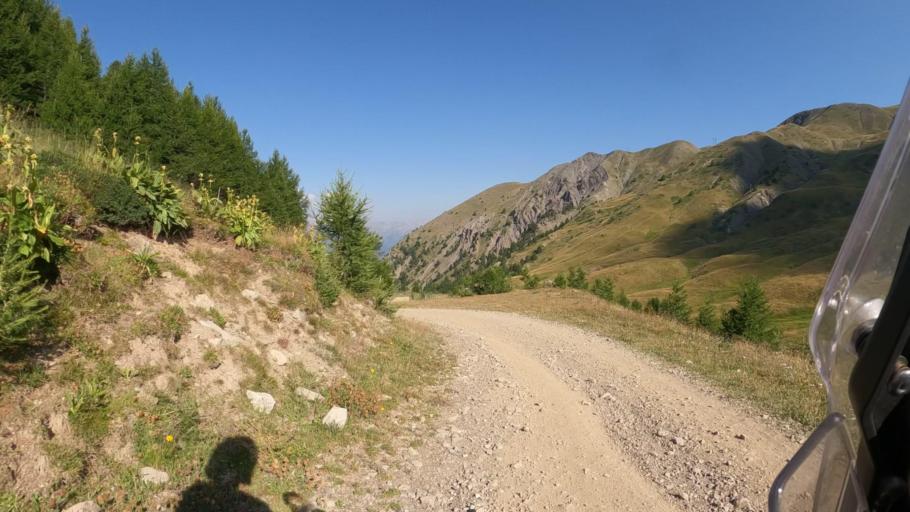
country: FR
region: Provence-Alpes-Cote d'Azur
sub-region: Departement des Hautes-Alpes
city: Guillestre
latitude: 44.5893
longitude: 6.6324
